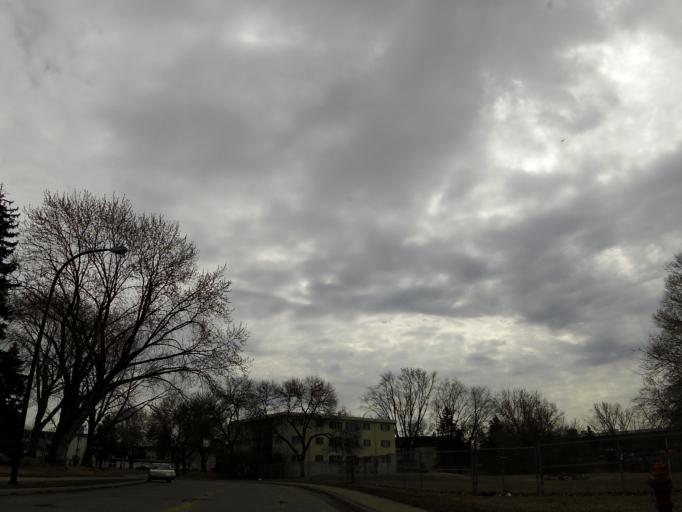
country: US
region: Minnesota
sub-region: Hennepin County
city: Edina
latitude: 44.8673
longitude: -93.3372
